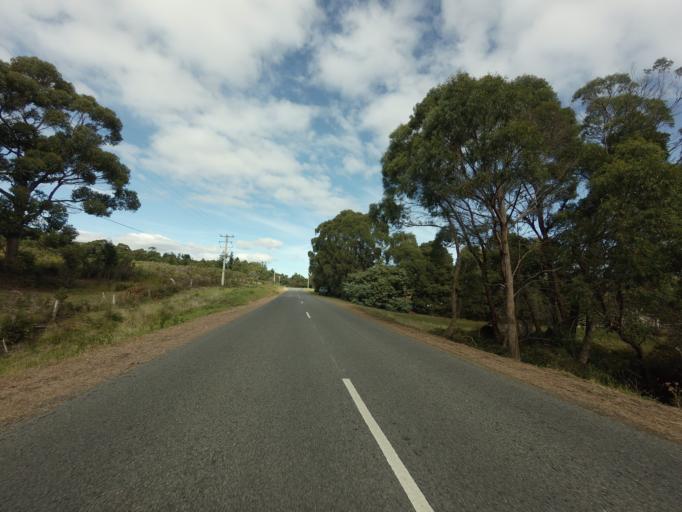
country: AU
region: Tasmania
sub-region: Clarence
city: Sandford
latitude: -43.0849
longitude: 147.7376
